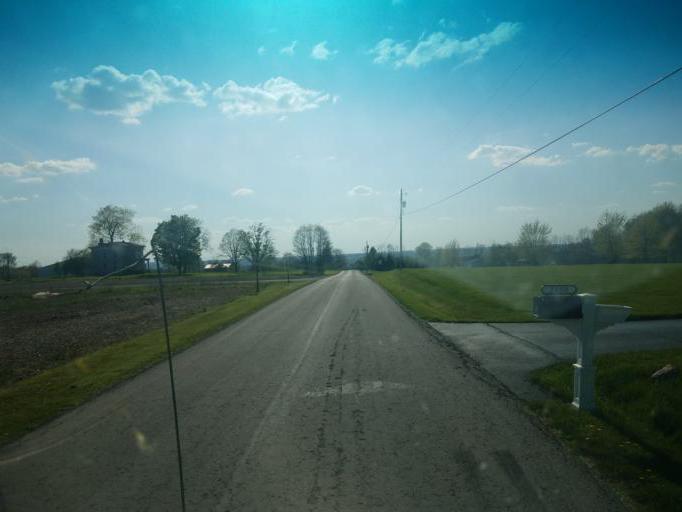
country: US
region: Ohio
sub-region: Wayne County
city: Wooster
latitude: 40.7480
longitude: -81.9108
